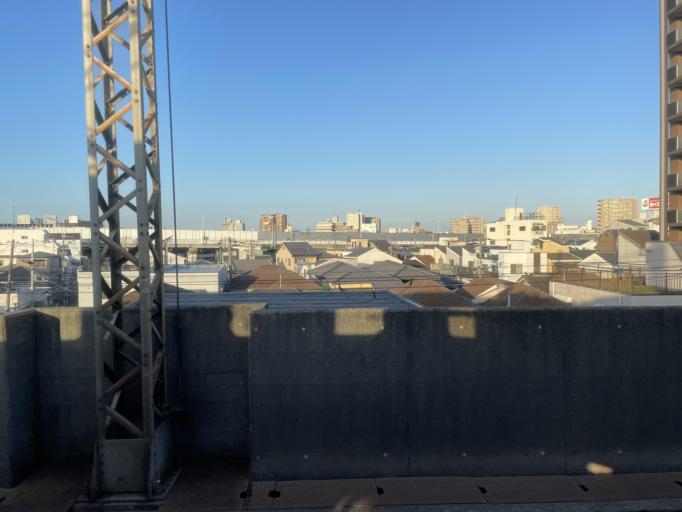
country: JP
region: Osaka
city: Matsubara
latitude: 34.6243
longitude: 135.5318
